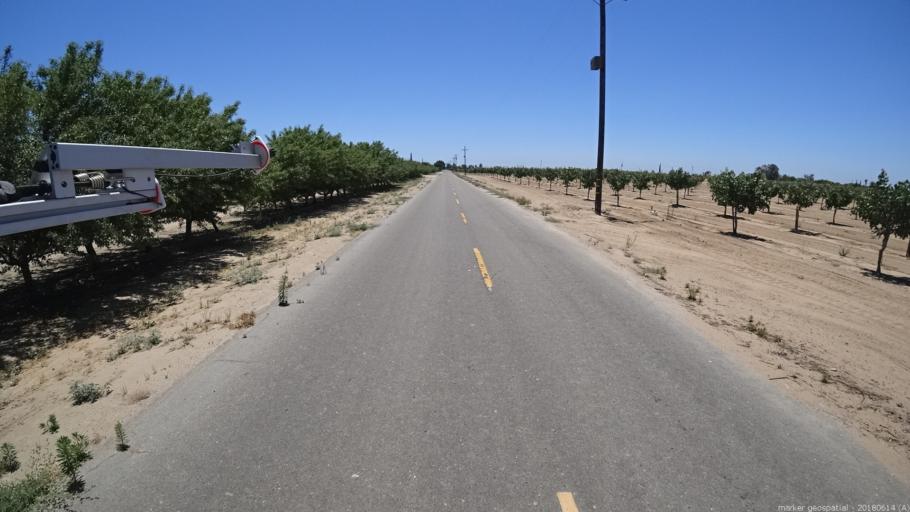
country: US
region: California
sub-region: Madera County
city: Fairmead
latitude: 37.0287
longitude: -120.1470
